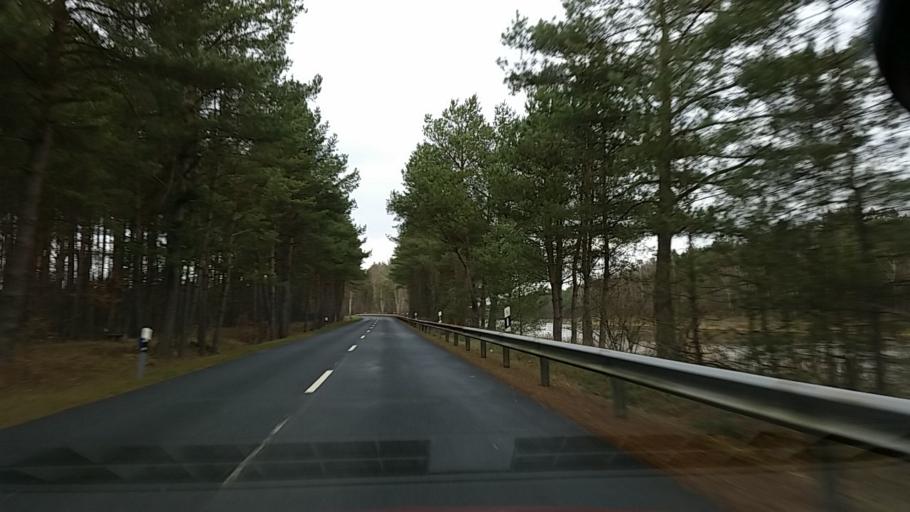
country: DE
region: Lower Saxony
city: Bodenteich
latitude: 52.8427
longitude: 10.6648
